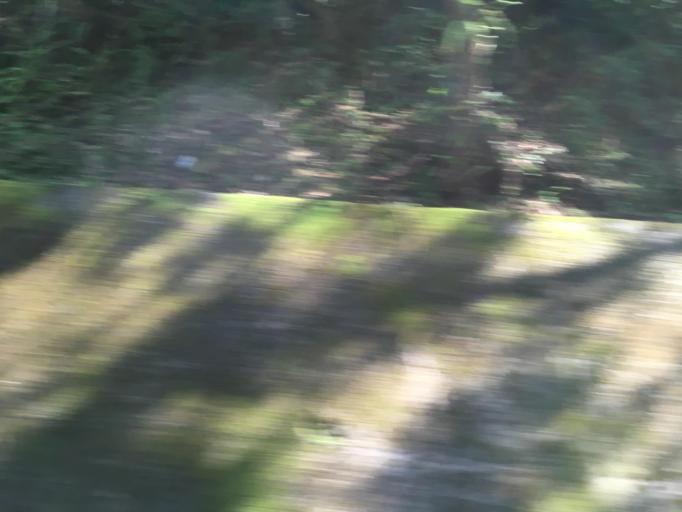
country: TW
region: Taiwan
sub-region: Yilan
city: Yilan
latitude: 24.7551
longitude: 121.5958
